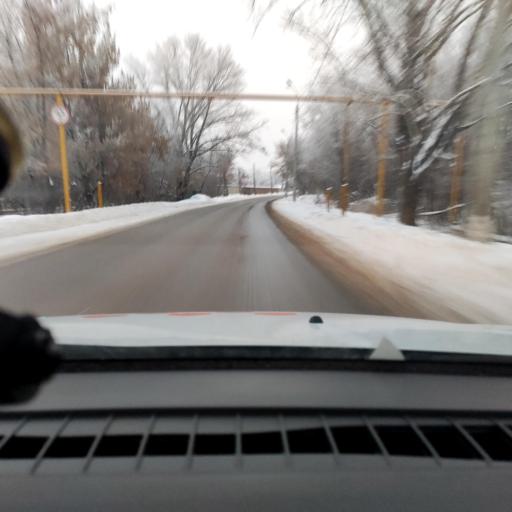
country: RU
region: Samara
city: Samara
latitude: 53.1333
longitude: 50.1511
